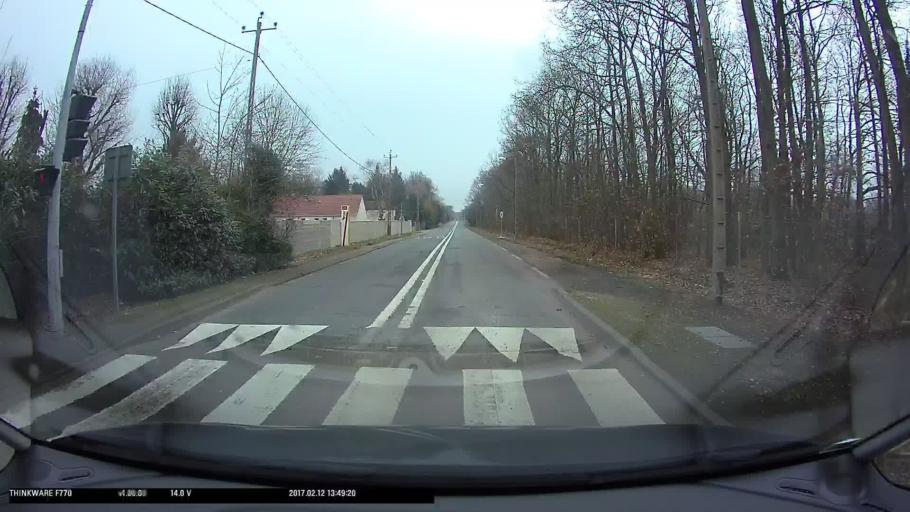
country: FR
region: Ile-de-France
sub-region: Departement des Yvelines
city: Triel-sur-Seine
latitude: 49.0006
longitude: 2.0138
